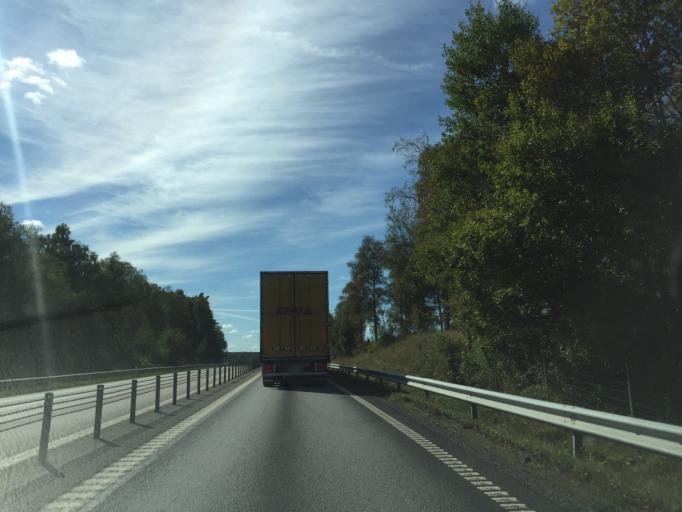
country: SE
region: Vaestmanland
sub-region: Kopings Kommun
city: Koping
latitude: 59.5331
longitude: 15.9875
